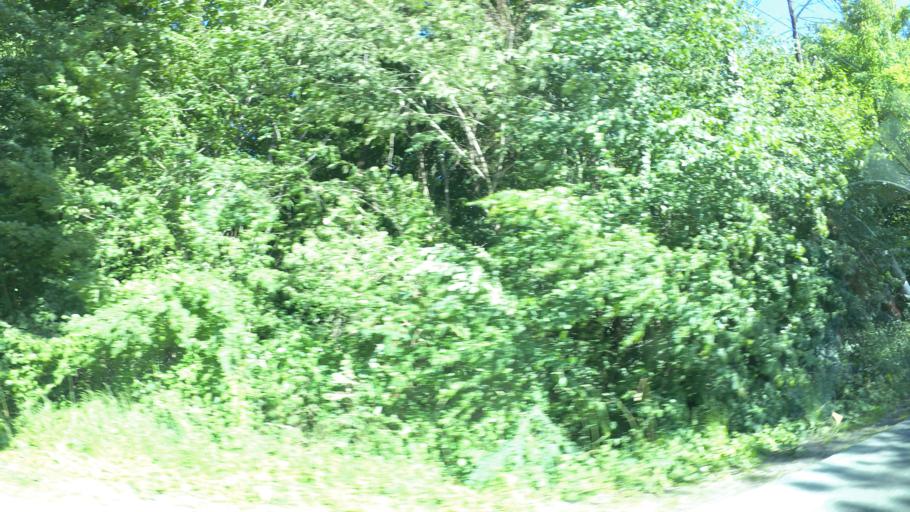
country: HR
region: Karlovacka
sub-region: Grad Karlovac
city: Slunj
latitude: 45.1300
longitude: 15.5775
